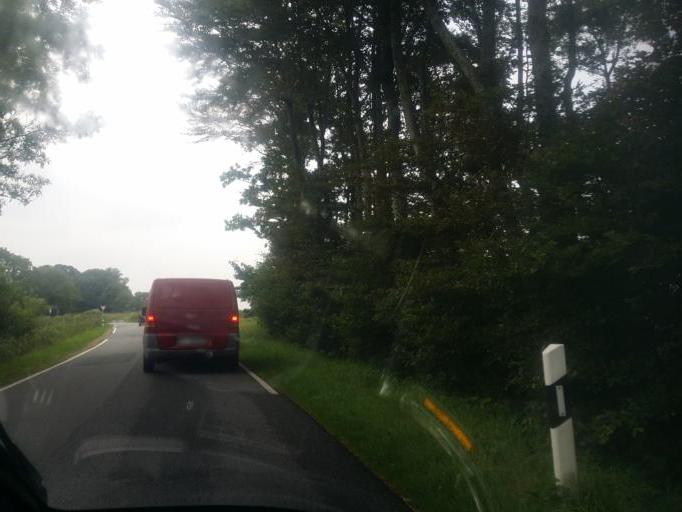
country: DE
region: Schleswig-Holstein
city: Koldenbuttel
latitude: 54.4204
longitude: 9.0524
